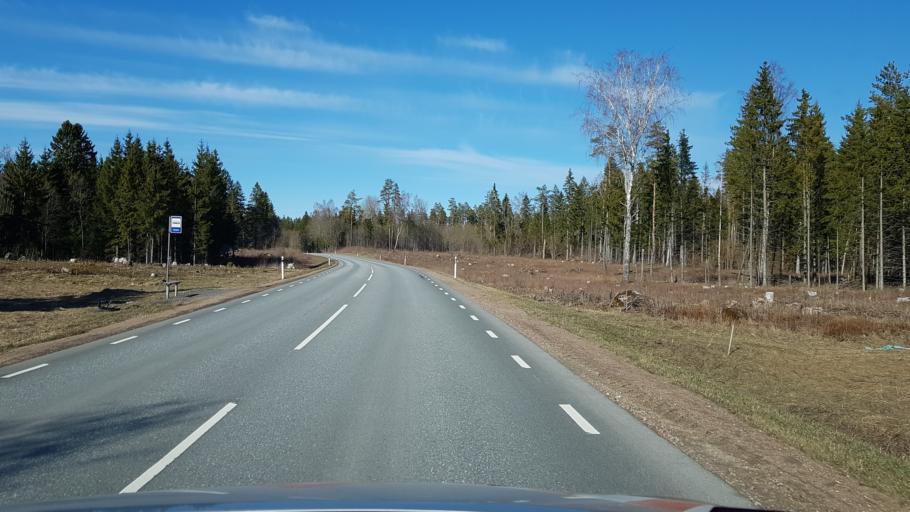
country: EE
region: Laeaene-Virumaa
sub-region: Tapa vald
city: Tapa
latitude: 59.3847
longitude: 26.0161
